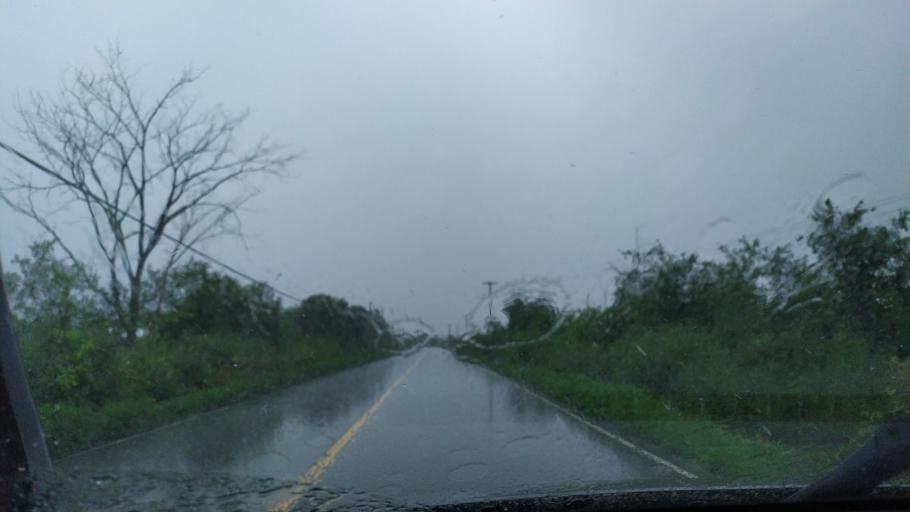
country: CA
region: Ontario
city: Prince Edward
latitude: 43.9715
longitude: -77.3923
